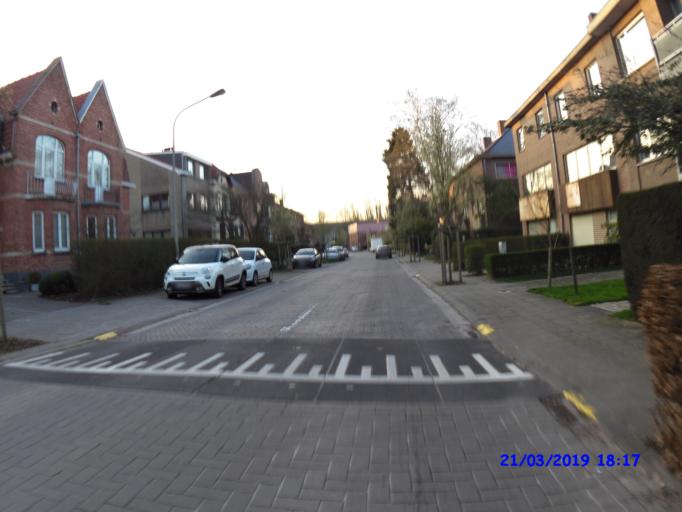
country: BE
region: Flanders
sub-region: Provincie Vlaams-Brabant
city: Linkebeek
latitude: 50.7757
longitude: 4.3308
